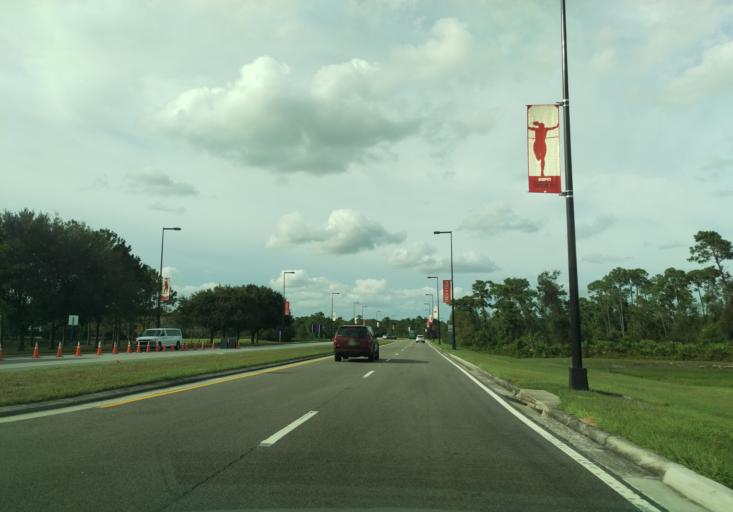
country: US
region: Florida
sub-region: Osceola County
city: Celebration
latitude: 28.3396
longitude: -81.5507
